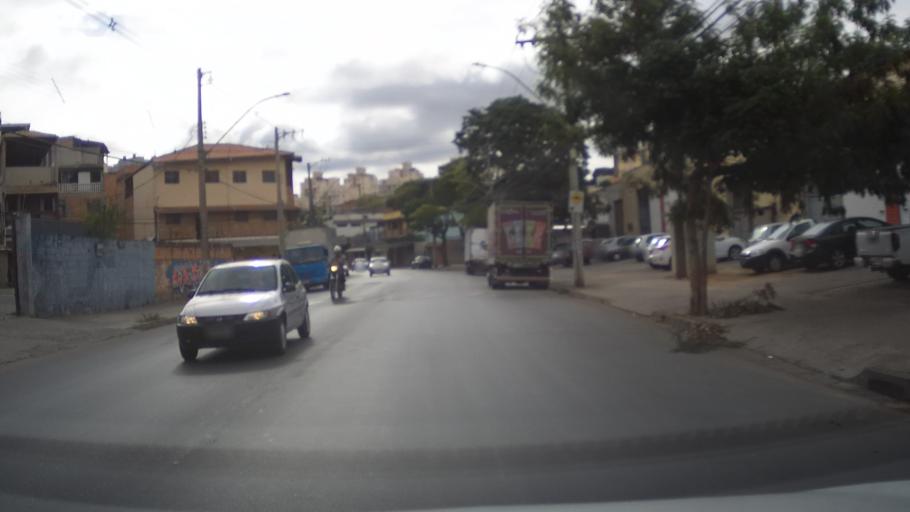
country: BR
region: Minas Gerais
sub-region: Belo Horizonte
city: Belo Horizonte
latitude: -19.8250
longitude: -43.9588
